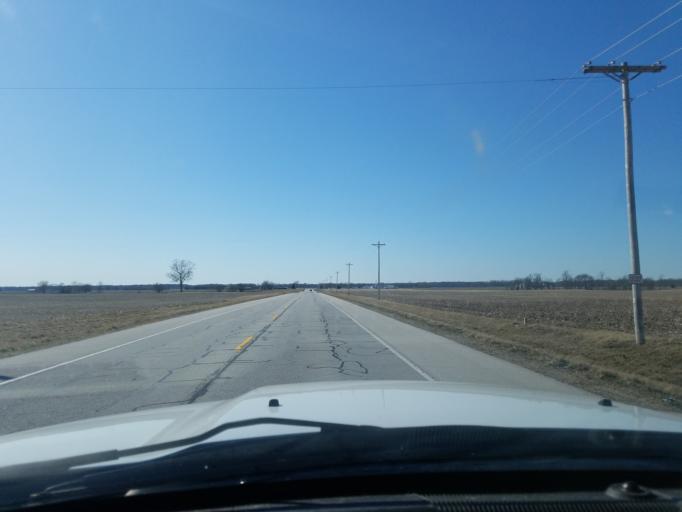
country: US
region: Indiana
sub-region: Shelby County
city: Shelbyville
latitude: 39.5043
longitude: -85.8264
